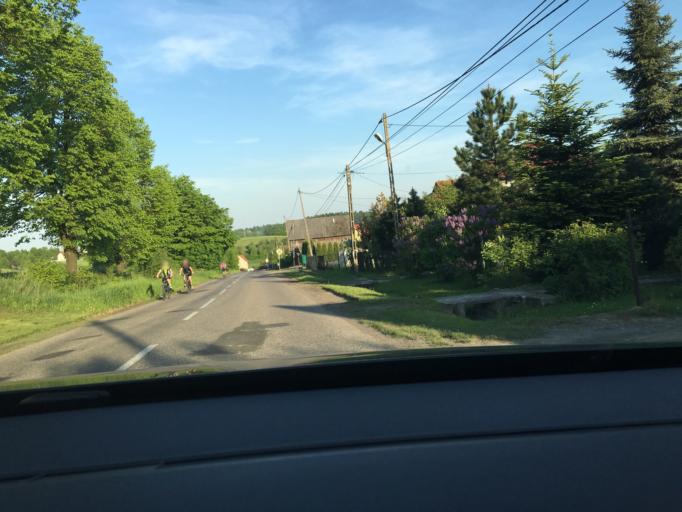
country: PL
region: Lesser Poland Voivodeship
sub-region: Powiat krakowski
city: Saspow
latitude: 50.2285
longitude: 19.7918
